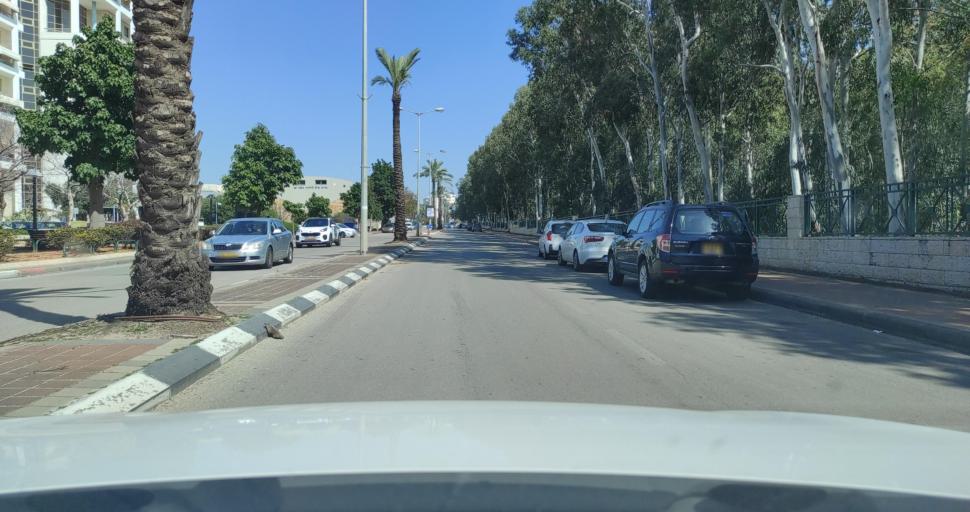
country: IL
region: Central District
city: Nordiyya
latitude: 32.3069
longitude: 34.8754
